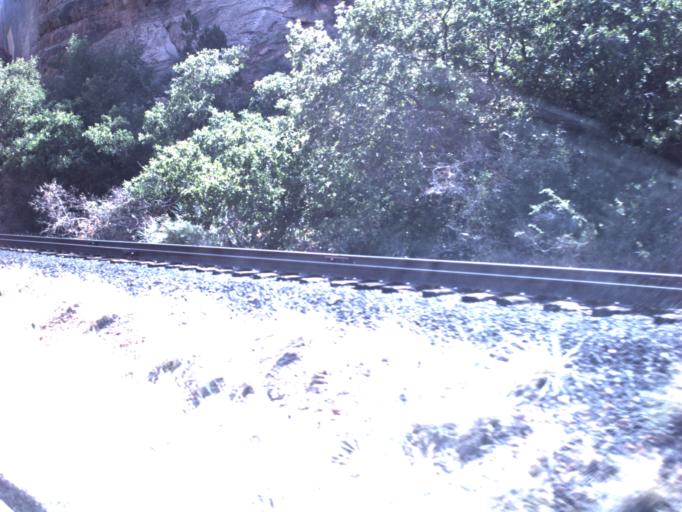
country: US
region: Utah
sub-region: Grand County
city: Moab
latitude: 38.5524
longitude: -109.6492
